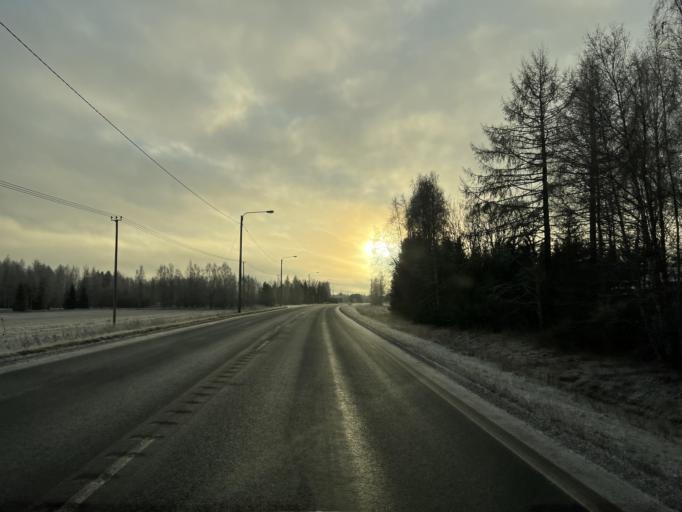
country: FI
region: Northern Ostrobothnia
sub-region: Oulu
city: Muhos
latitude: 64.8589
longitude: 25.8922
